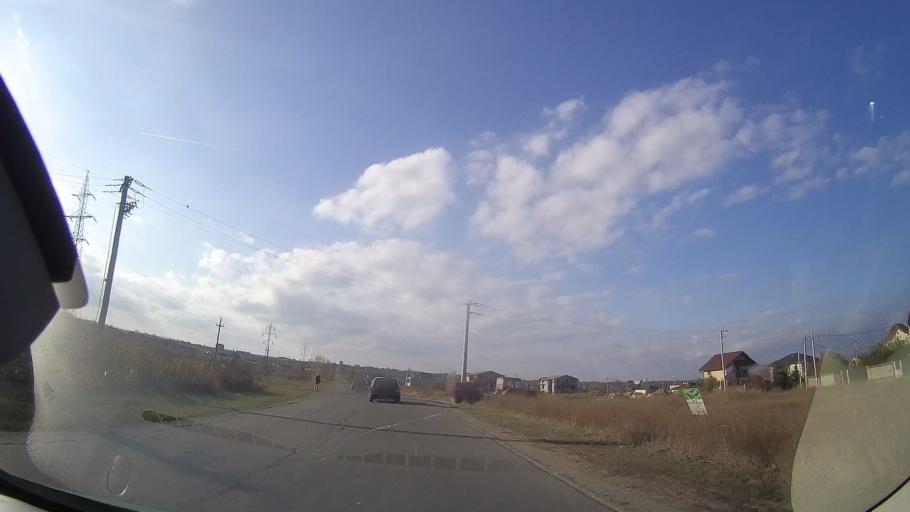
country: RO
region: Constanta
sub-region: Comuna Limanu
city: Limanu
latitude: 43.7934
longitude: 28.5436
